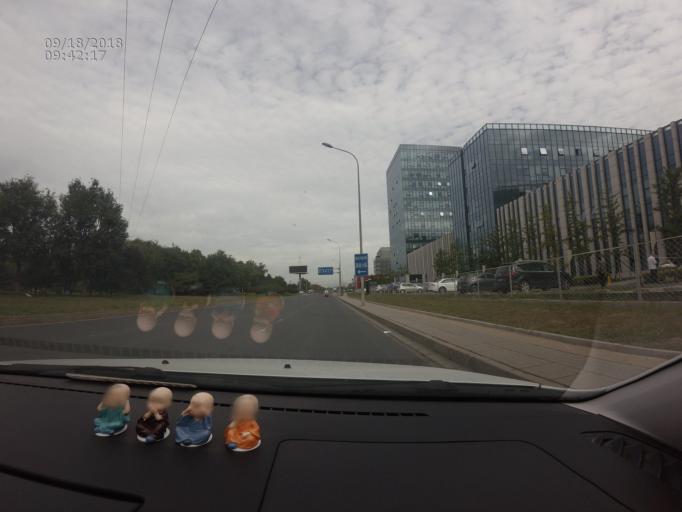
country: CN
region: Beijing
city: Xibeiwang
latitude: 40.0706
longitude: 116.2392
